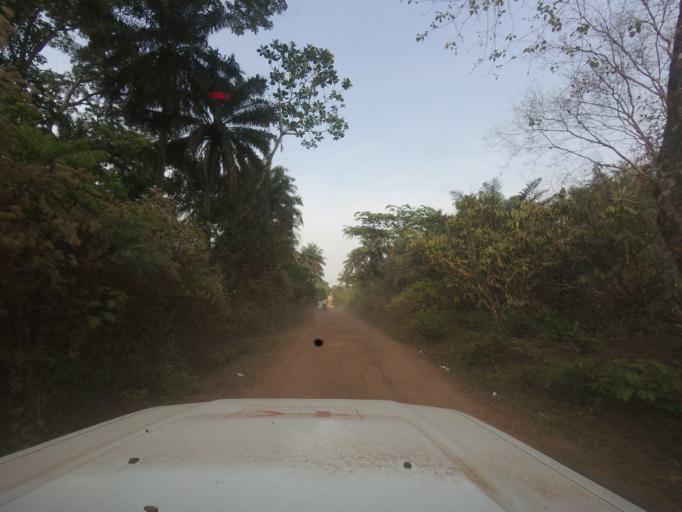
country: GN
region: Nzerekore
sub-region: Prefecture de Guekedou
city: Gueckedou
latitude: 8.5243
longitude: -10.1835
